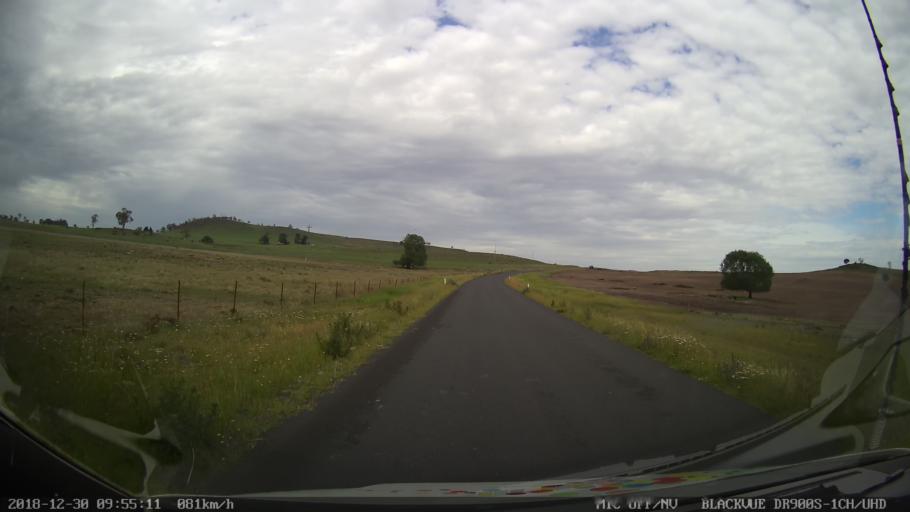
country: AU
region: New South Wales
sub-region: Cooma-Monaro
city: Cooma
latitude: -36.5200
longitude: 149.2680
